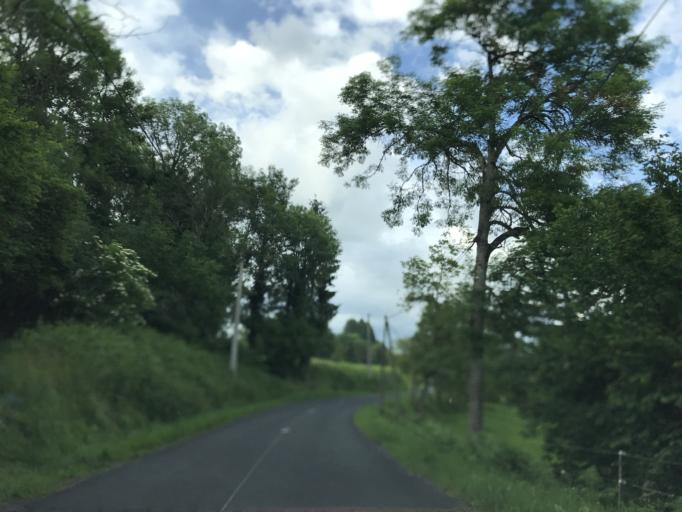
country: FR
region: Auvergne
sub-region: Departement du Puy-de-Dome
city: Escoutoux
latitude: 45.8099
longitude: 3.6101
